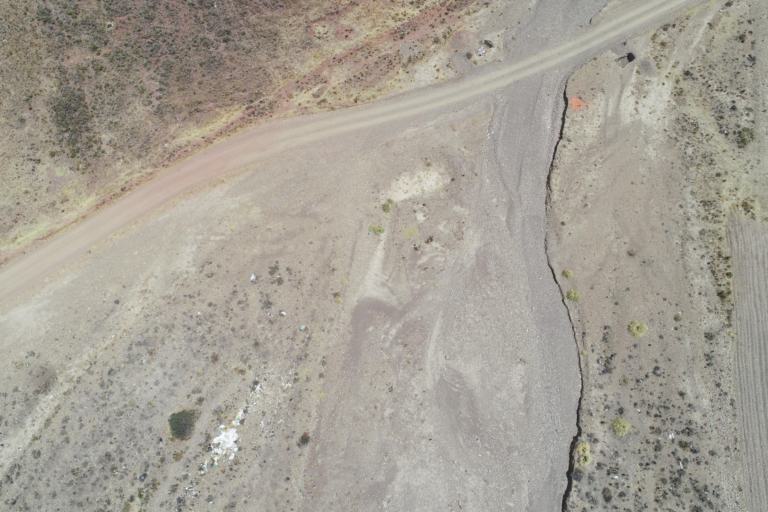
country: BO
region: La Paz
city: Achacachi
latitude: -15.9099
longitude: -68.8827
